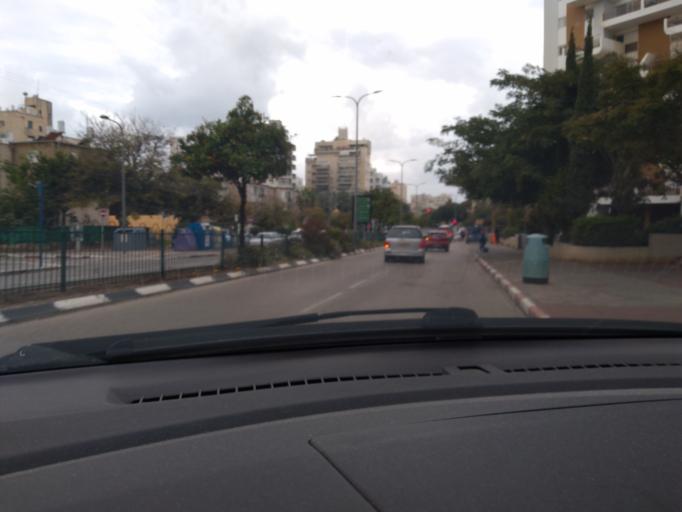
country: IL
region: Central District
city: Netanya
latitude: 32.3421
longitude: 34.8616
